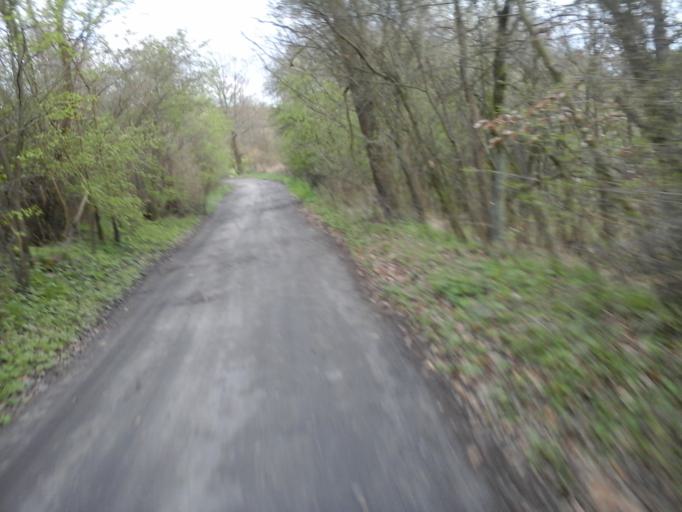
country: PL
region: West Pomeranian Voivodeship
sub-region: Powiat choszczenski
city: Krzecin
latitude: 53.0700
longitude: 15.5801
